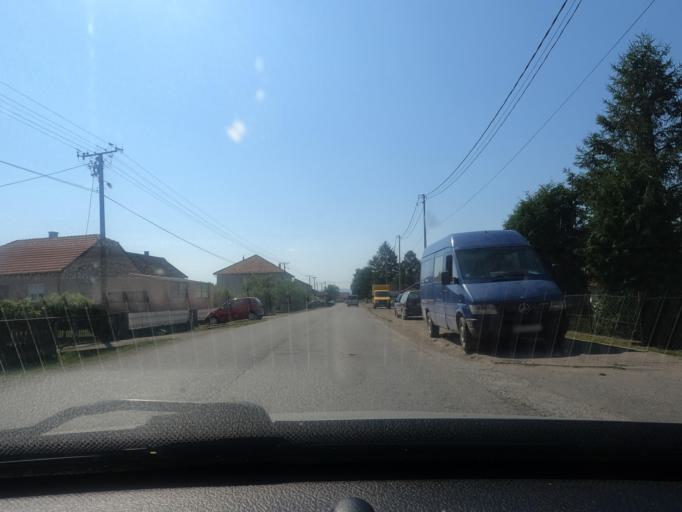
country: RS
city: Lipnicki Sor
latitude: 44.5805
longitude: 19.2642
